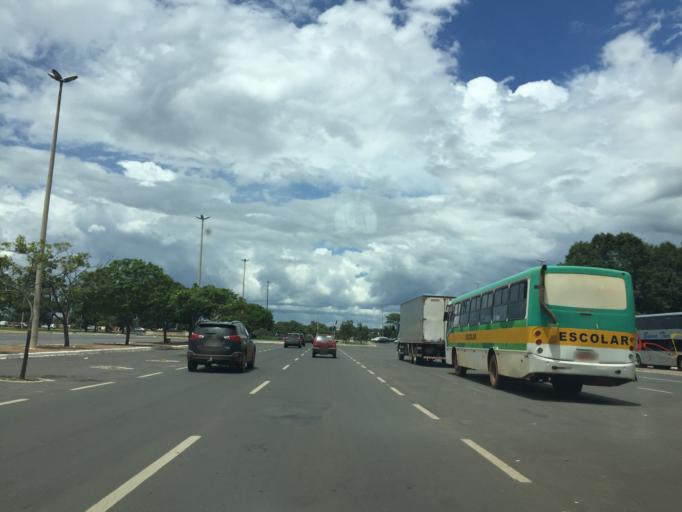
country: BR
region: Federal District
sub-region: Brasilia
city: Brasilia
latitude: -15.7900
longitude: -47.8957
